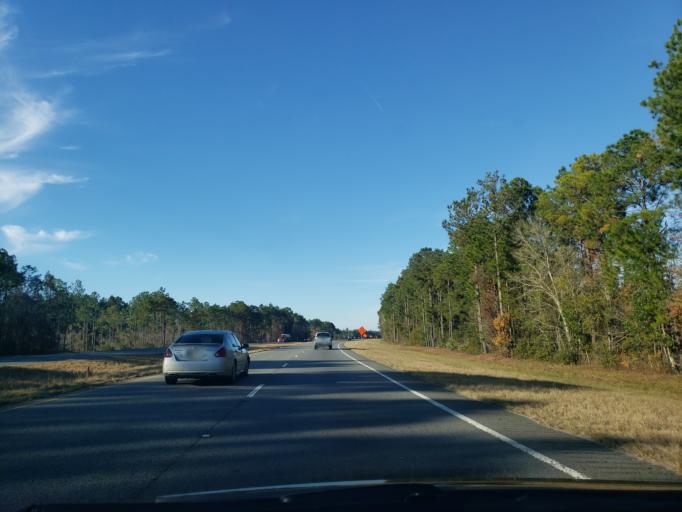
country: US
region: Georgia
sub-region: Ware County
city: Deenwood
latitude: 31.2184
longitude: -82.4224
